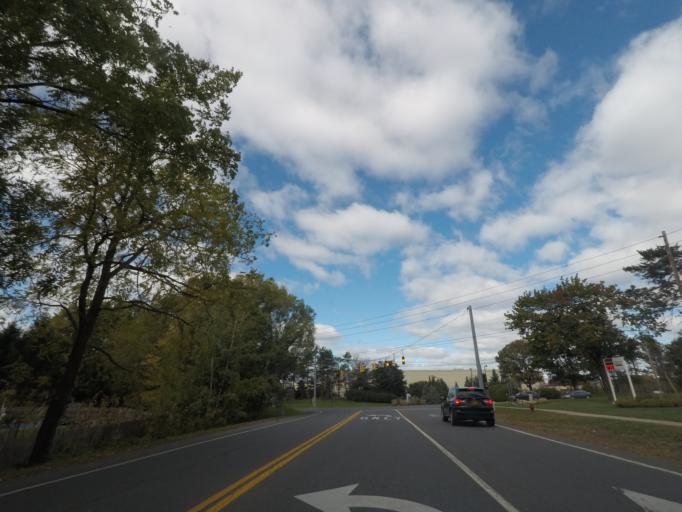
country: US
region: New York
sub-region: Saratoga County
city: Country Knolls
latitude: 42.8553
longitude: -73.7771
